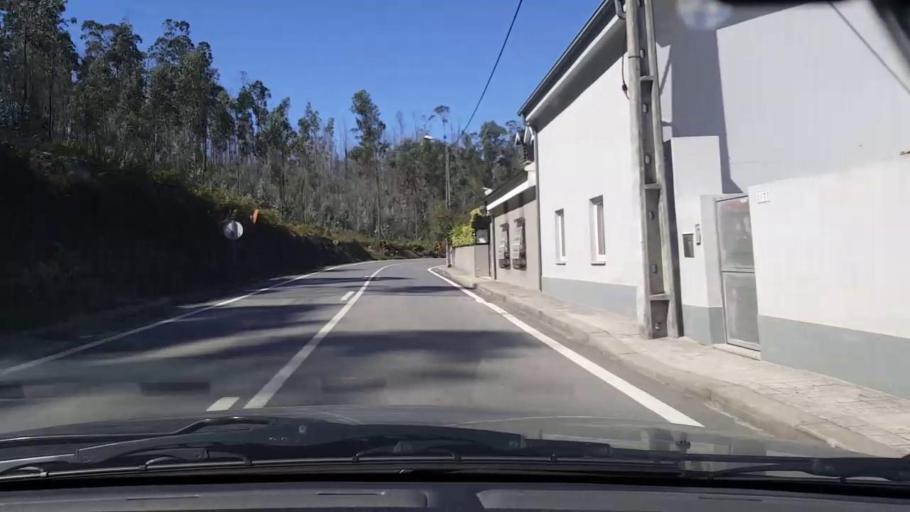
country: PT
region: Porto
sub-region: Vila do Conde
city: Arvore
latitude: 41.3420
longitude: -8.6550
